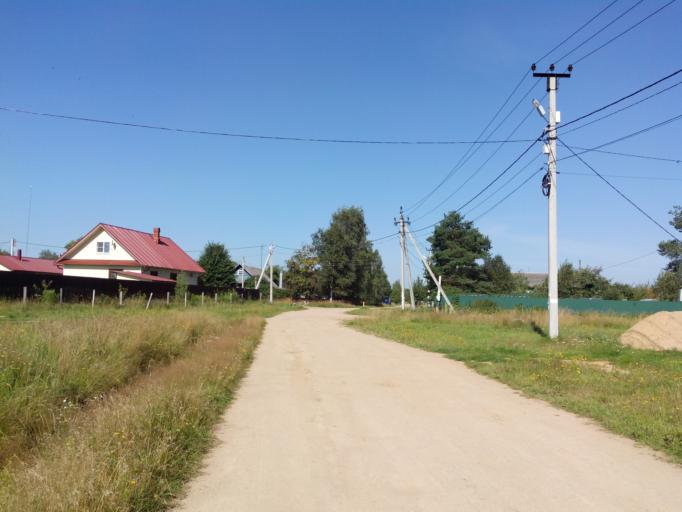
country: RU
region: Moskovskaya
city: Verbilki
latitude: 56.5412
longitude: 37.6170
